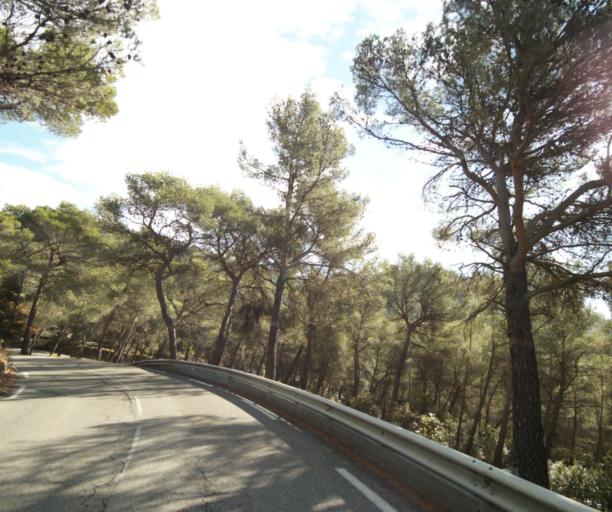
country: FR
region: Provence-Alpes-Cote d'Azur
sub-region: Departement des Bouches-du-Rhone
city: Ceyreste
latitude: 43.2311
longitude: 5.6571
